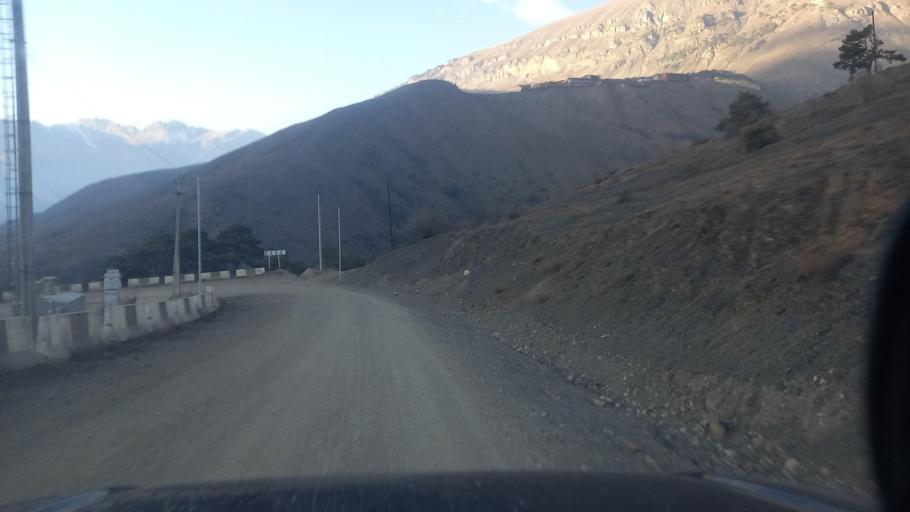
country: RU
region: Ingushetiya
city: Dzhayrakh
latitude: 42.8200
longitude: 44.7033
